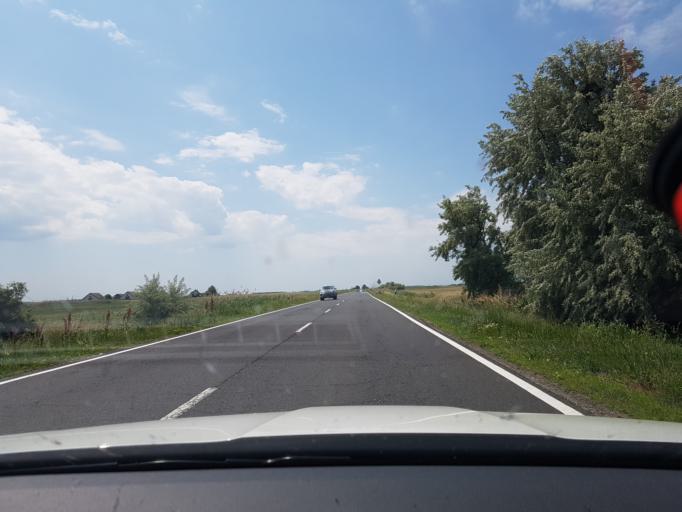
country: HU
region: Hajdu-Bihar
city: Egyek
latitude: 47.5705
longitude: 20.9870
